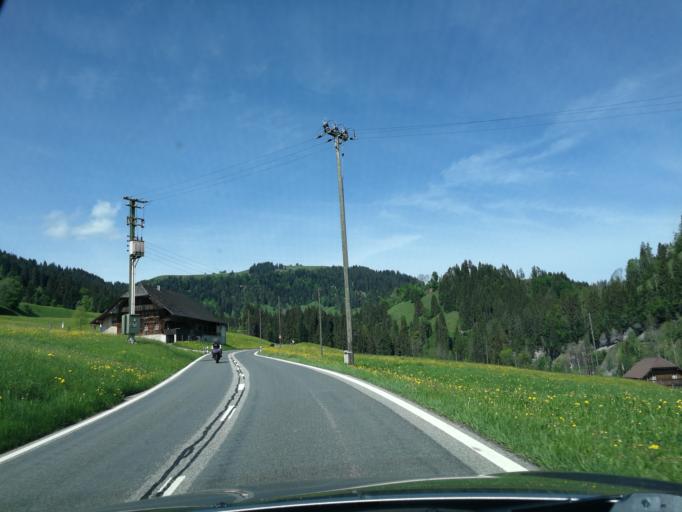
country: CH
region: Bern
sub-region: Emmental District
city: Wald
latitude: 46.8202
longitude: 7.8428
